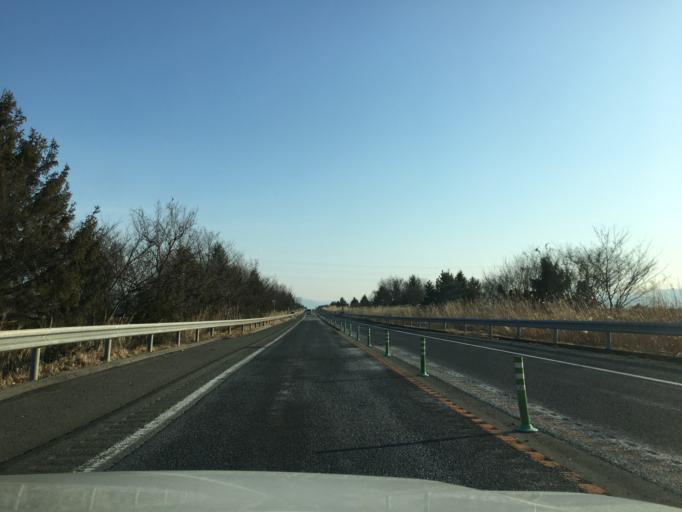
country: JP
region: Yamagata
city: Sagae
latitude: 38.3433
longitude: 140.2972
